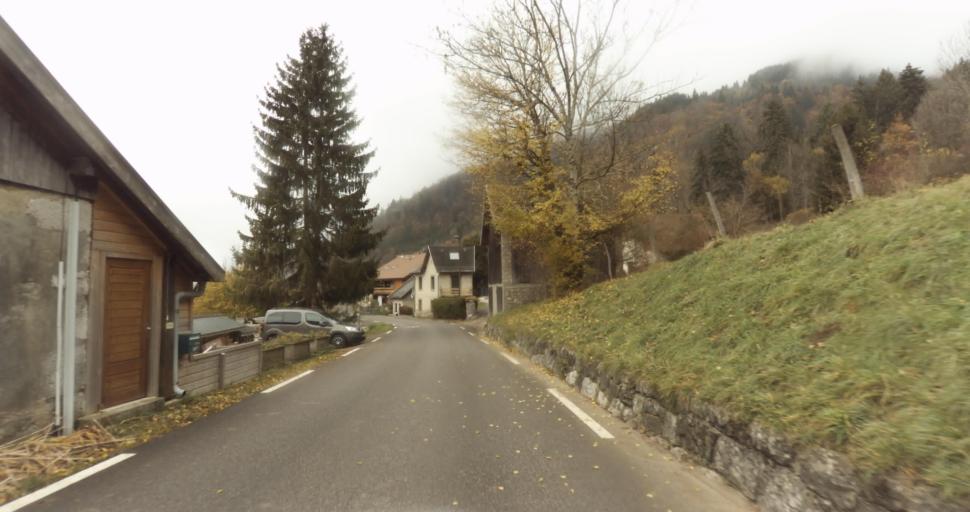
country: FR
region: Rhone-Alpes
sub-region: Departement de la Haute-Savoie
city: Thorens-Glieres
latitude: 45.9836
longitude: 6.2819
